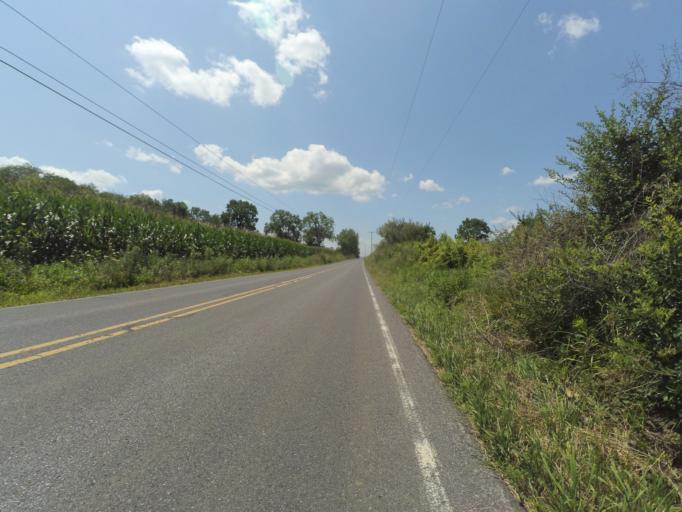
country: US
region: Pennsylvania
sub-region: Centre County
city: Centre Hall
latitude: 40.8202
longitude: -77.7289
